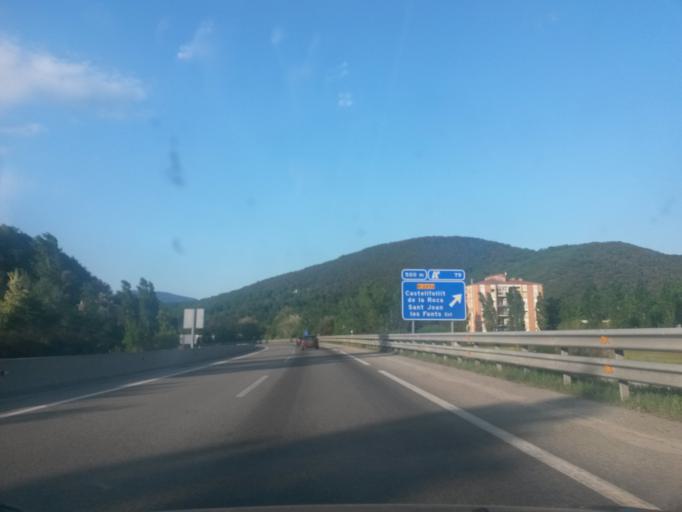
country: ES
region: Catalonia
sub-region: Provincia de Girona
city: Sant Joan les Fonts
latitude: 42.2013
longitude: 2.5349
